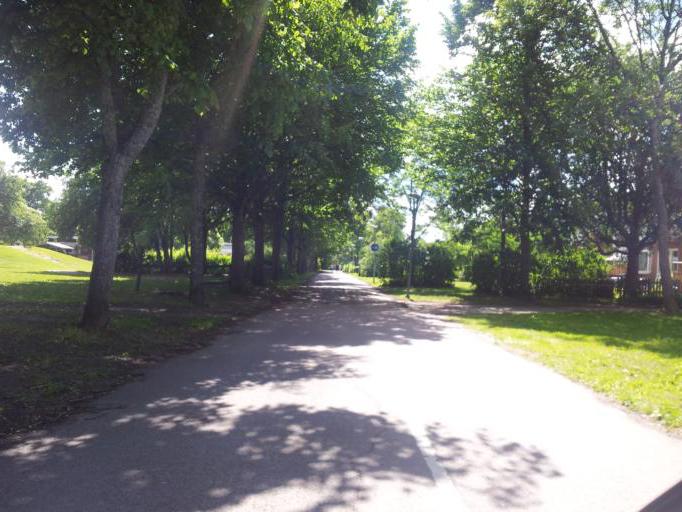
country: SE
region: Uppsala
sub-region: Uppsala Kommun
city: Uppsala
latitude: 59.8697
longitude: 17.6529
